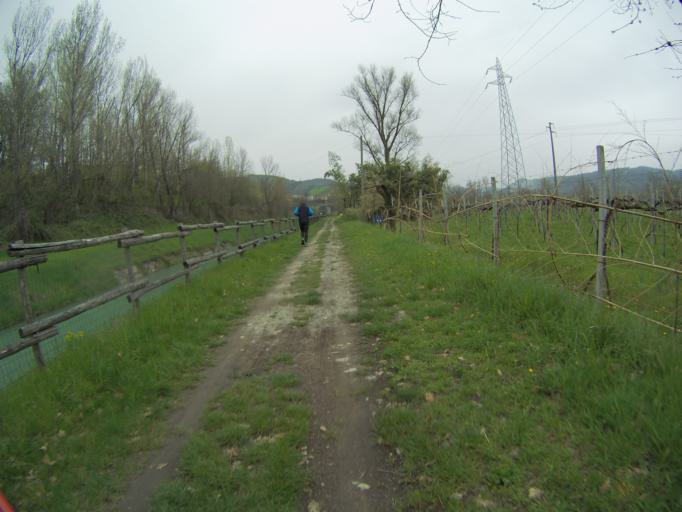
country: IT
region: Emilia-Romagna
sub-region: Provincia di Reggio Emilia
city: Ciano d'Enza
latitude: 44.5989
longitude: 10.4053
